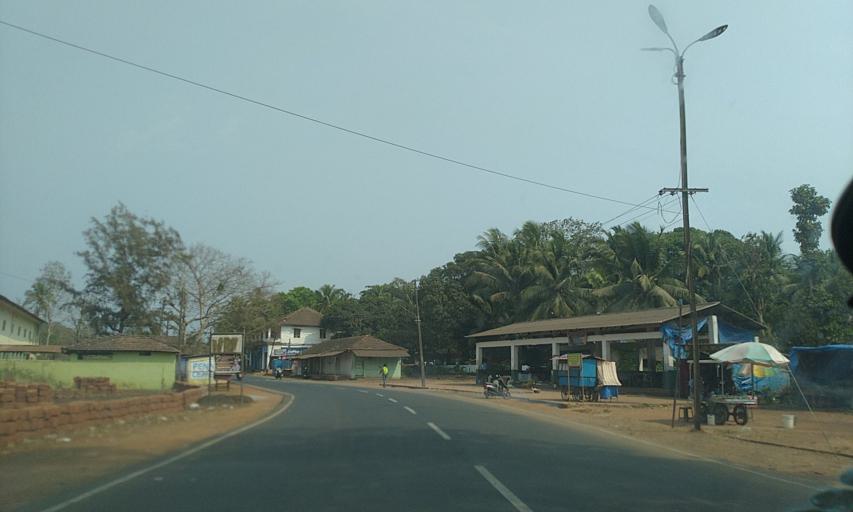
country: IN
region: Goa
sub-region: South Goa
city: Davorlim
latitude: 15.2611
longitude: 74.0448
